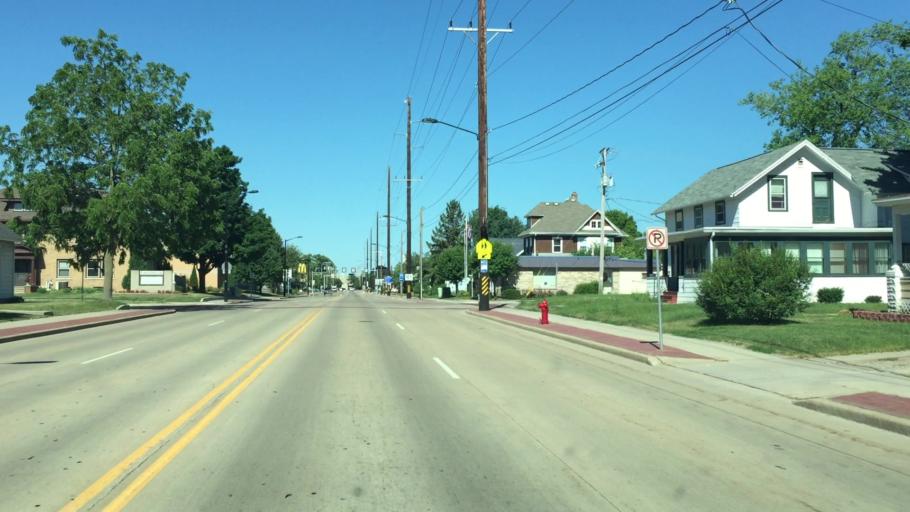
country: US
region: Wisconsin
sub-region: Winnebago County
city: Menasha
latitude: 44.2047
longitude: -88.4424
